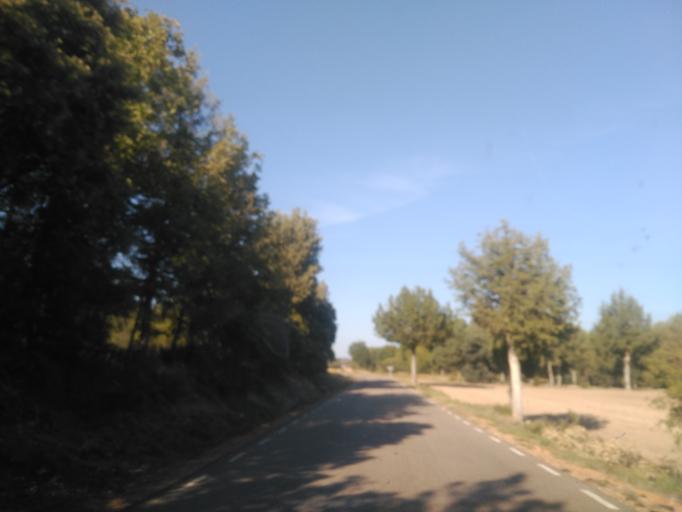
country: ES
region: Castille and Leon
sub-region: Provincia de Burgos
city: Brazacorta
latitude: 41.7013
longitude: -3.3945
